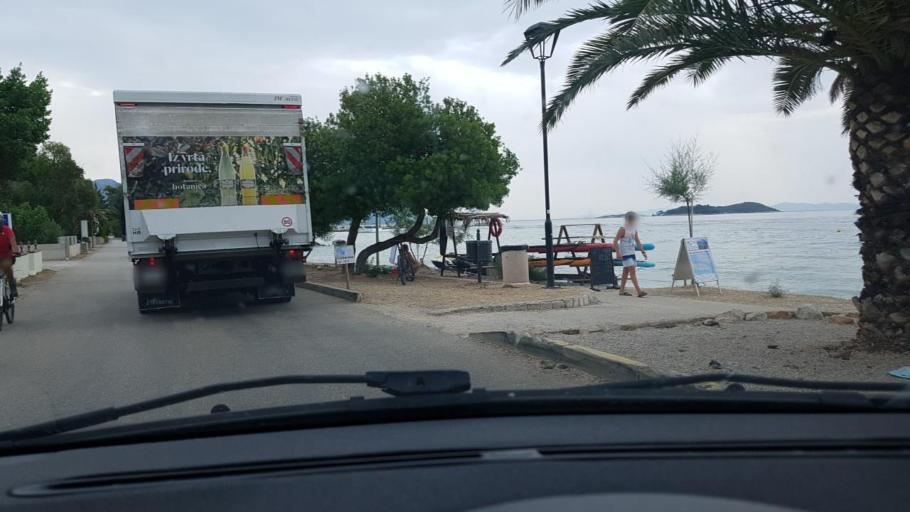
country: HR
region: Dubrovacko-Neretvanska
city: Orebic
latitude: 42.9749
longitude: 17.1688
